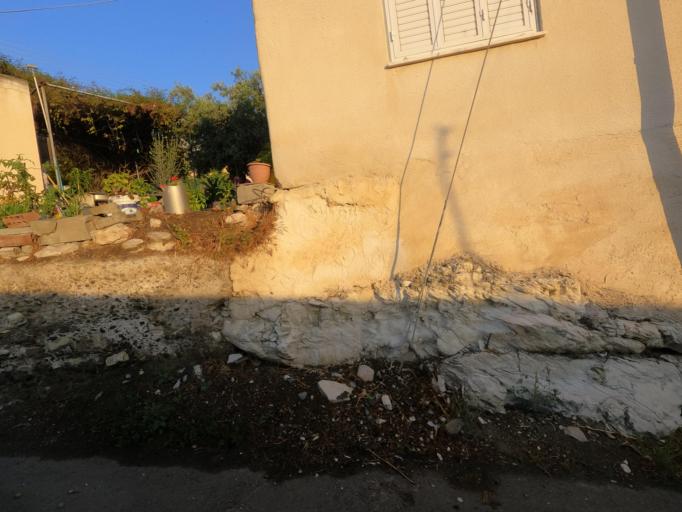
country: CY
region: Lefkosia
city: Alampra
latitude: 34.9884
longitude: 33.3977
